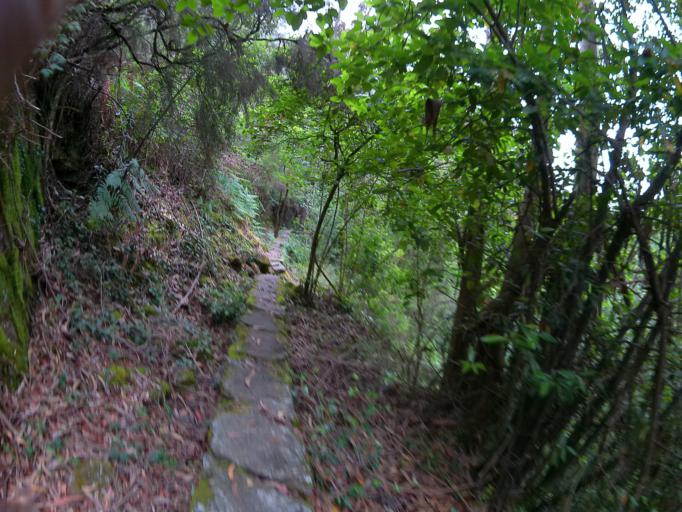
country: PT
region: Aveiro
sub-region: Albergaria-A-Velha
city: Branca
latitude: 40.7500
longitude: -8.4299
